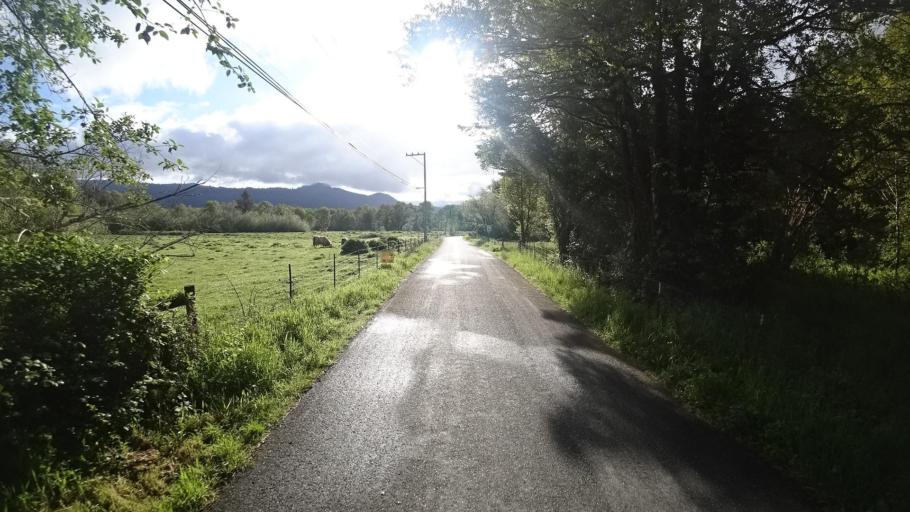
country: US
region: California
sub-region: Humboldt County
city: Blue Lake
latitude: 40.8821
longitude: -124.0188
